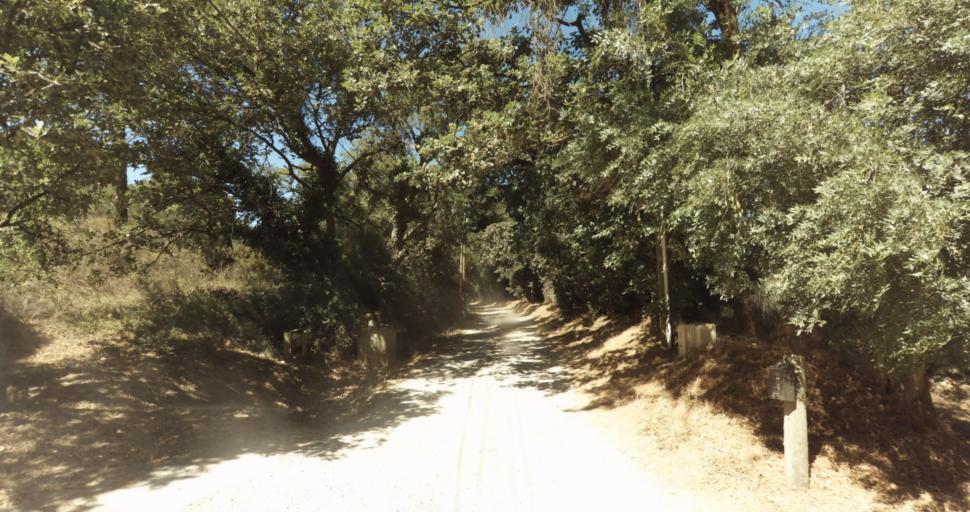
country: FR
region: Provence-Alpes-Cote d'Azur
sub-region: Departement du Var
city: Gassin
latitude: 43.2370
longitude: 6.5670
